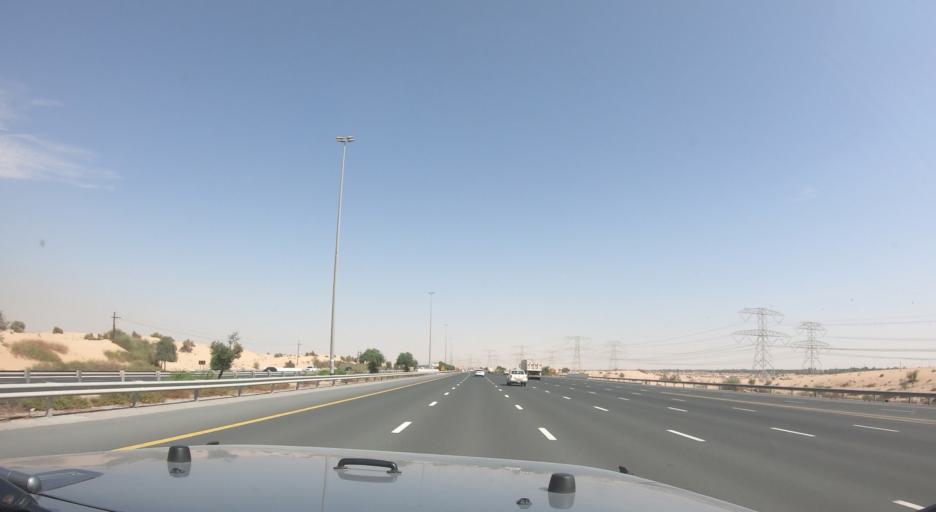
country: AE
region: Ash Shariqah
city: Sharjah
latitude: 25.1687
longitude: 55.5022
